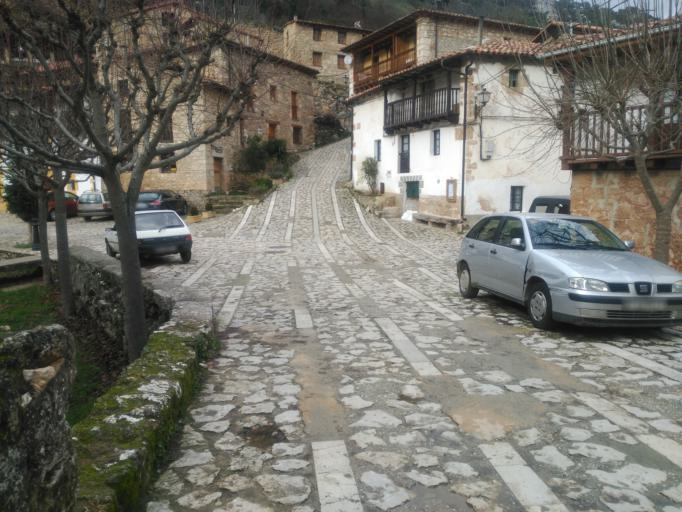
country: ES
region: Cantabria
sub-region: Provincia de Cantabria
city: San Martin de Elines
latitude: 42.8340
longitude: -3.7935
